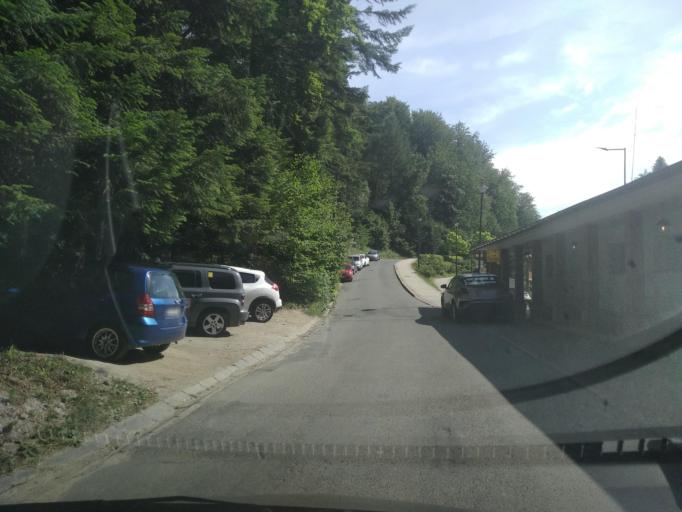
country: PL
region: Subcarpathian Voivodeship
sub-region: Powiat krosnienski
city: Iwonicz-Zdroj
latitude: 49.5584
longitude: 21.7876
